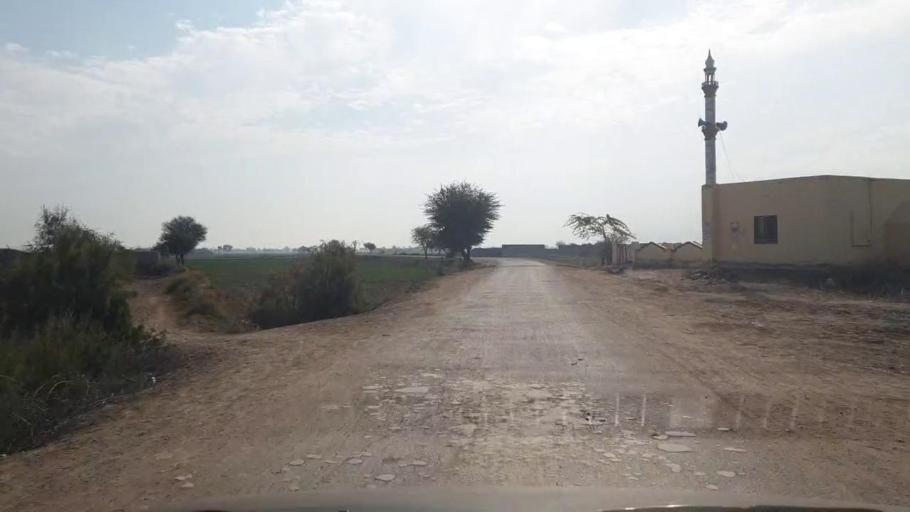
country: PK
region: Sindh
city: Hala
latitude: 26.0006
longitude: 68.4060
